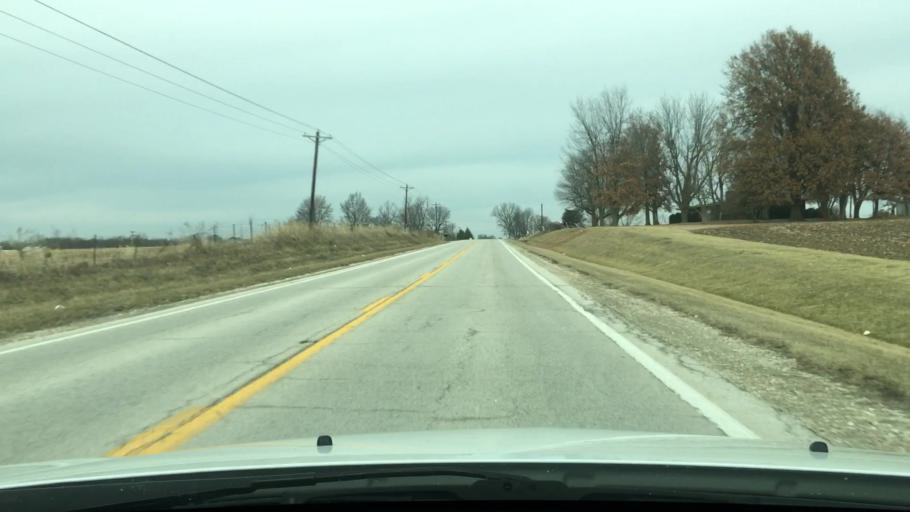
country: US
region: Illinois
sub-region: Pike County
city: Pittsfield
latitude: 39.5523
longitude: -90.9165
